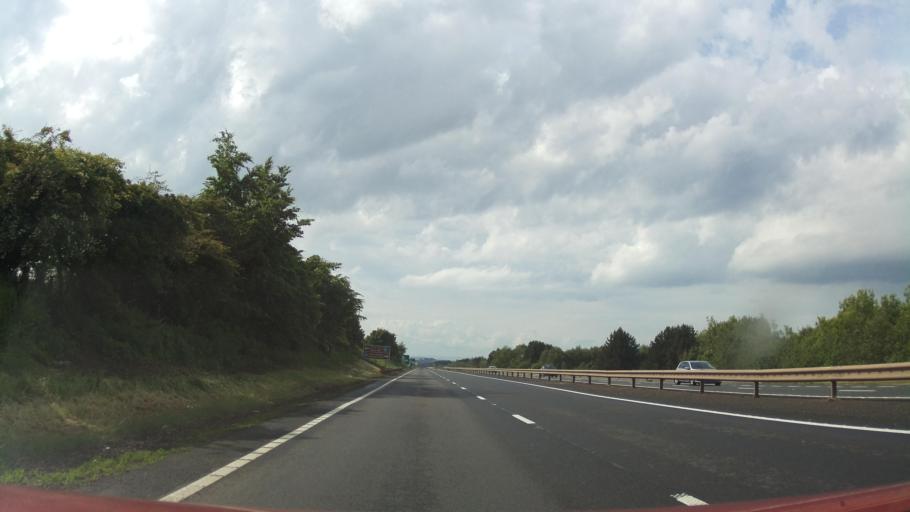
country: GB
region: Scotland
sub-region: East Lothian
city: Dunbar
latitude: 55.9744
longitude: -2.4728
